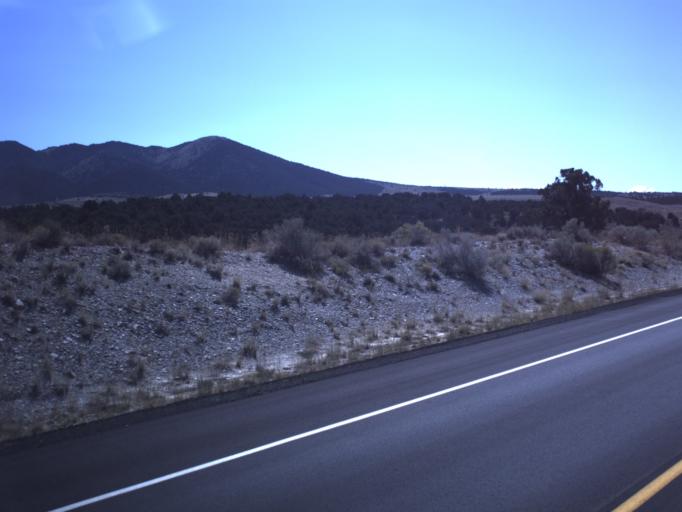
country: US
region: Utah
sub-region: Utah County
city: Eagle Mountain
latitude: 40.0200
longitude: -112.2799
